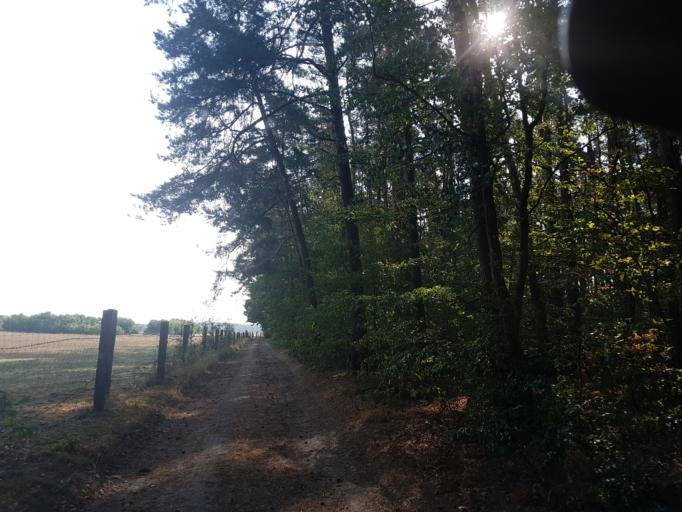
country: DE
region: Brandenburg
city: Wiesenburg
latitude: 52.0620
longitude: 12.3676
